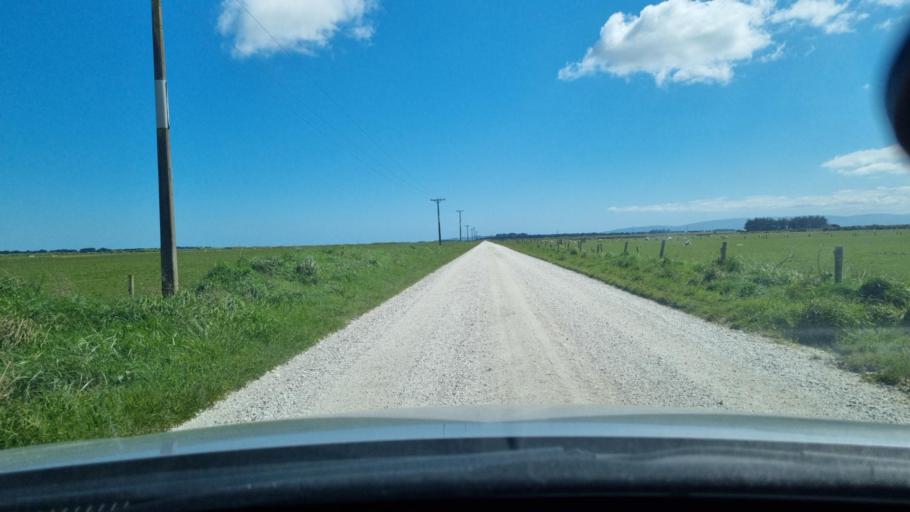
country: NZ
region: Southland
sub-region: Invercargill City
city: Invercargill
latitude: -46.3694
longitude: 168.2670
